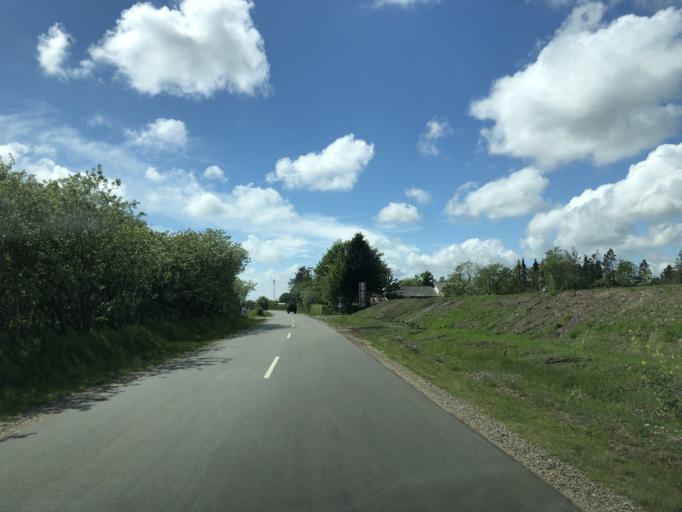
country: DK
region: Central Jutland
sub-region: Ringkobing-Skjern Kommune
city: Skjern
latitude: 55.9430
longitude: 8.5259
